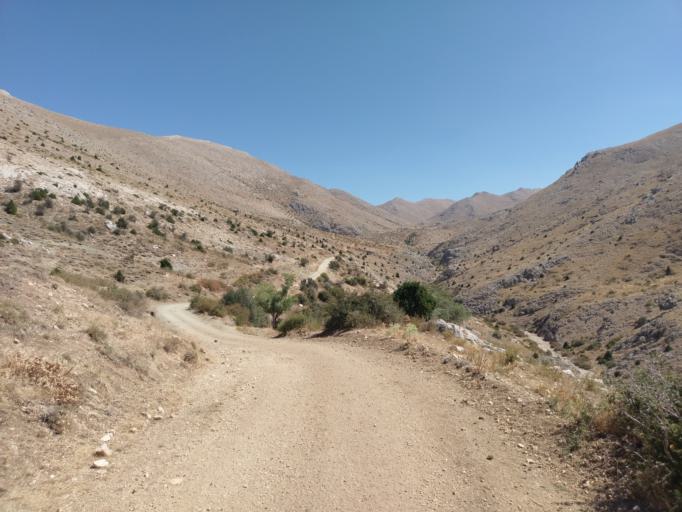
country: TR
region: Kayseri
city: Toklar
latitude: 38.4266
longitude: 36.1461
